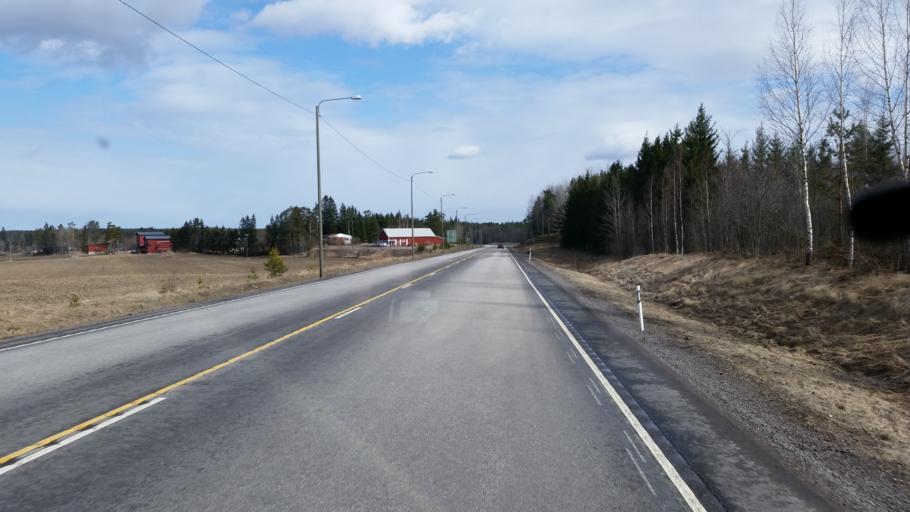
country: FI
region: Uusimaa
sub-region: Loviisa
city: Liljendal
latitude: 60.5629
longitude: 26.0578
